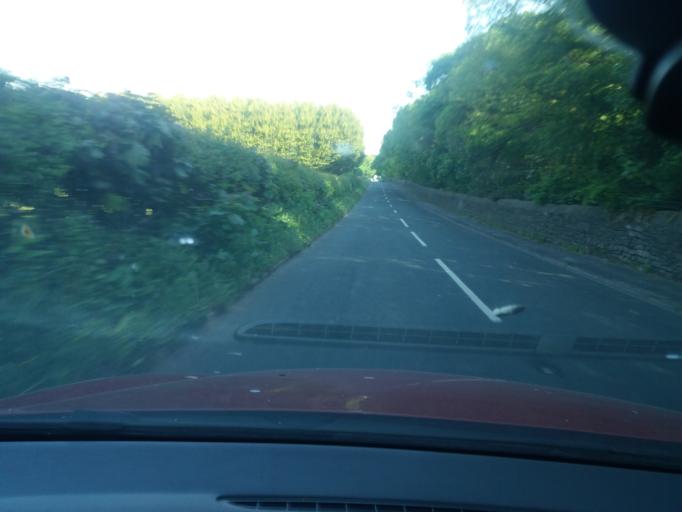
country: GB
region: England
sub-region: Borough of Wigan
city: Haigh
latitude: 53.6180
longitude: -2.5807
